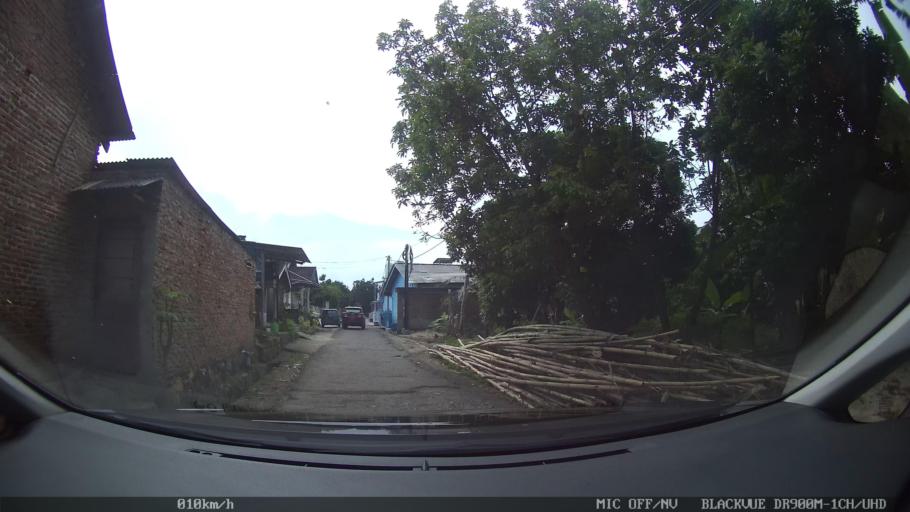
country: ID
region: Lampung
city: Kedaton
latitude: -5.3865
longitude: 105.2132
